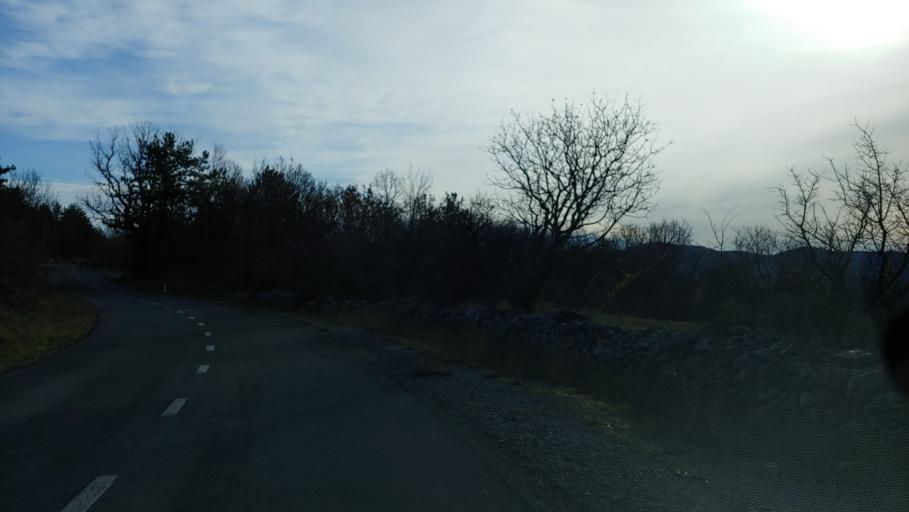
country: SI
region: Komen
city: Komen
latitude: 45.8064
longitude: 13.7049
